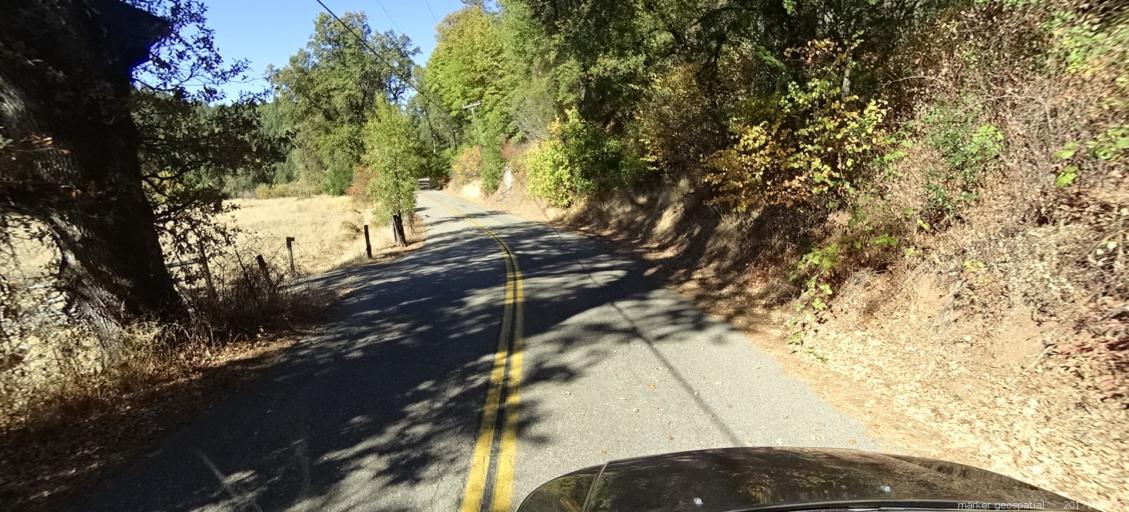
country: US
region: California
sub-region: Shasta County
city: Bella Vista
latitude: 40.7485
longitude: -122.0204
